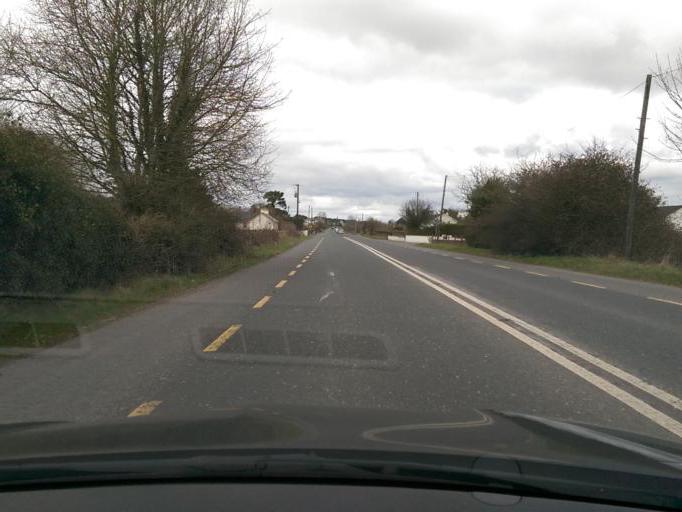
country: IE
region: Leinster
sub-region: An Iarmhi
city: Athlone
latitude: 53.3939
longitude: -7.9907
